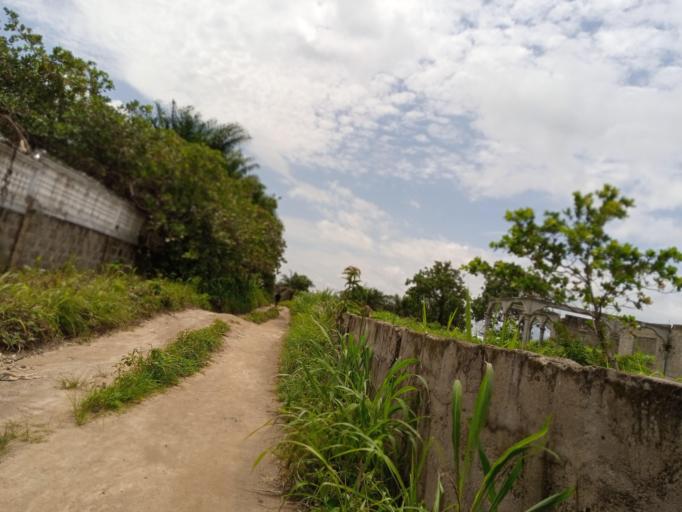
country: SL
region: Northern Province
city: Masoyila
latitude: 8.5545
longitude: -13.1605
